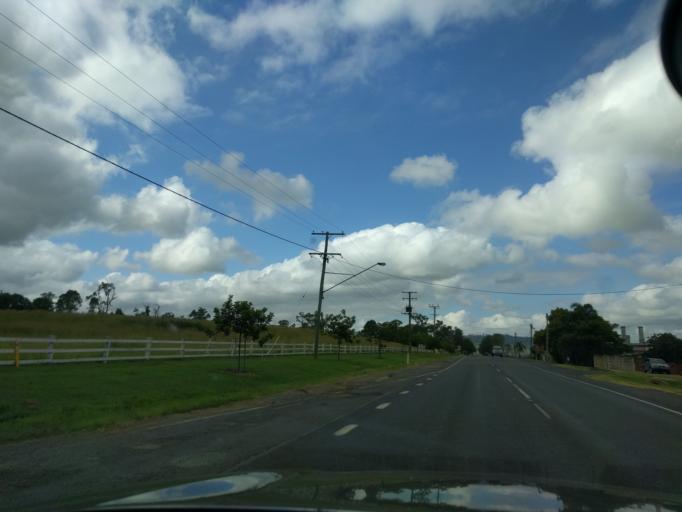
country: AU
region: Queensland
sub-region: Logan
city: Cedar Vale
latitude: -27.9975
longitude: 152.9886
